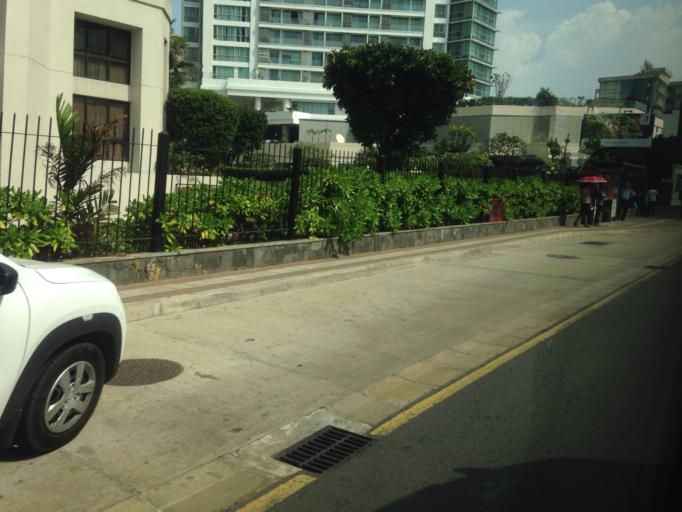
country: LK
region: Western
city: Colombo
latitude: 6.9179
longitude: 79.8476
